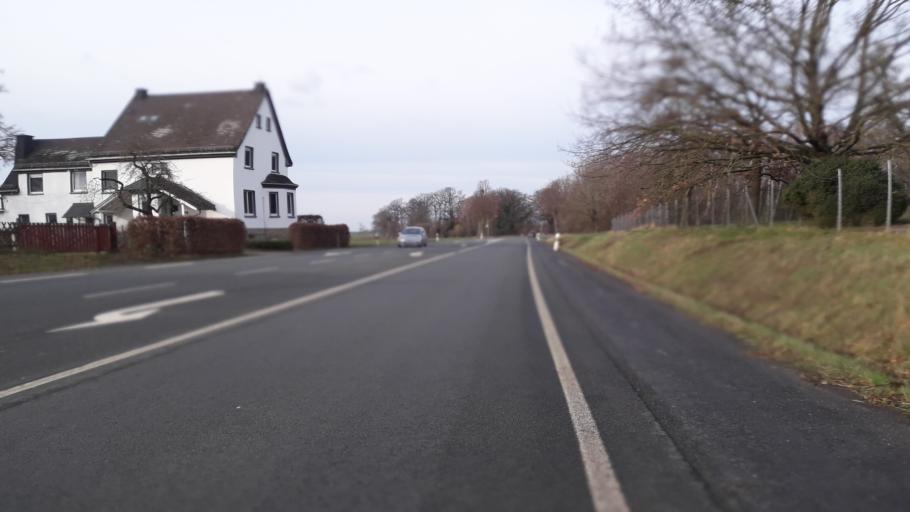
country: DE
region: North Rhine-Westphalia
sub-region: Regierungsbezirk Arnsberg
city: Soest
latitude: 51.5886
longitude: 8.0830
